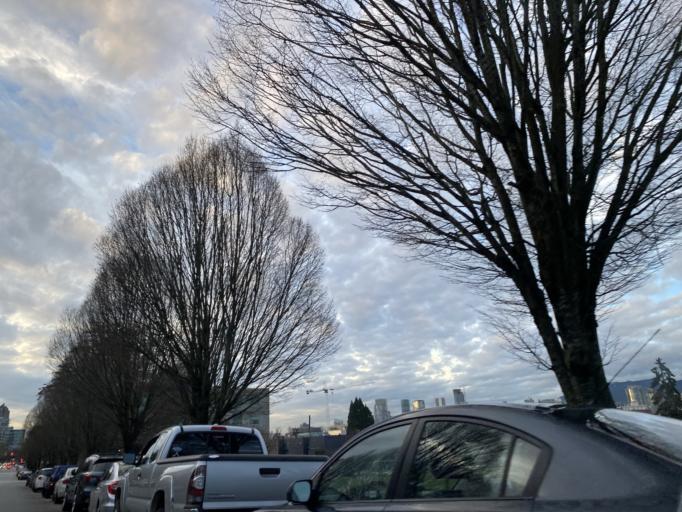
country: CA
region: British Columbia
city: Vancouver
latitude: 49.2639
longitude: -123.1080
